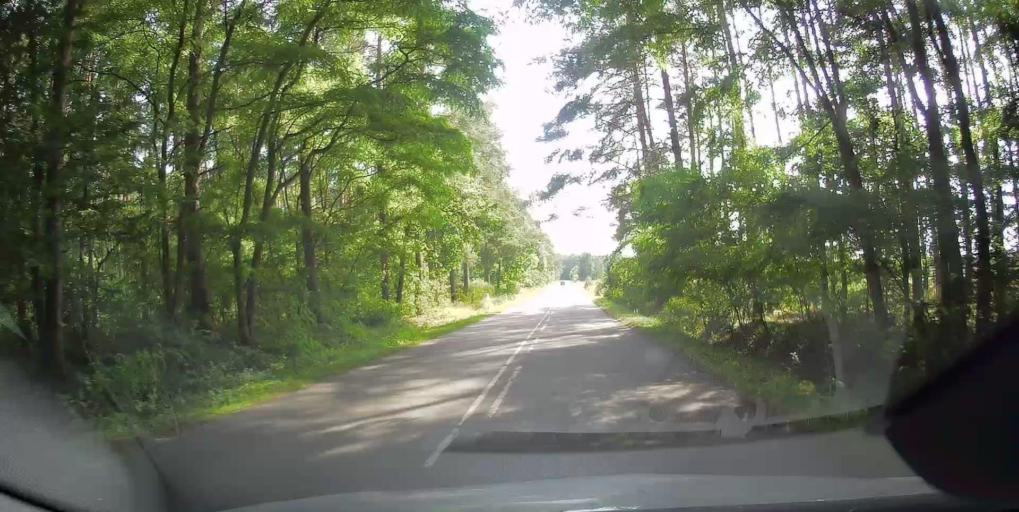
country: PL
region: Lodz Voivodeship
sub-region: Powiat opoczynski
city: Mniszkow
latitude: 51.4050
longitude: 20.0429
